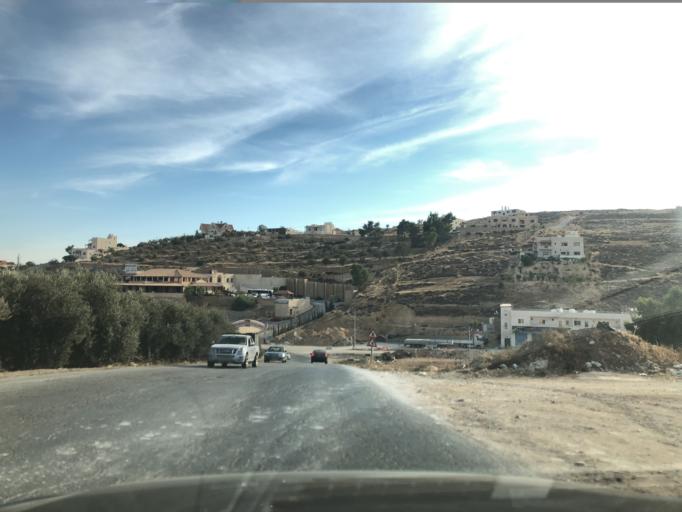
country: JO
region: Jerash
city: Jarash
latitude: 32.2688
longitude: 35.8871
